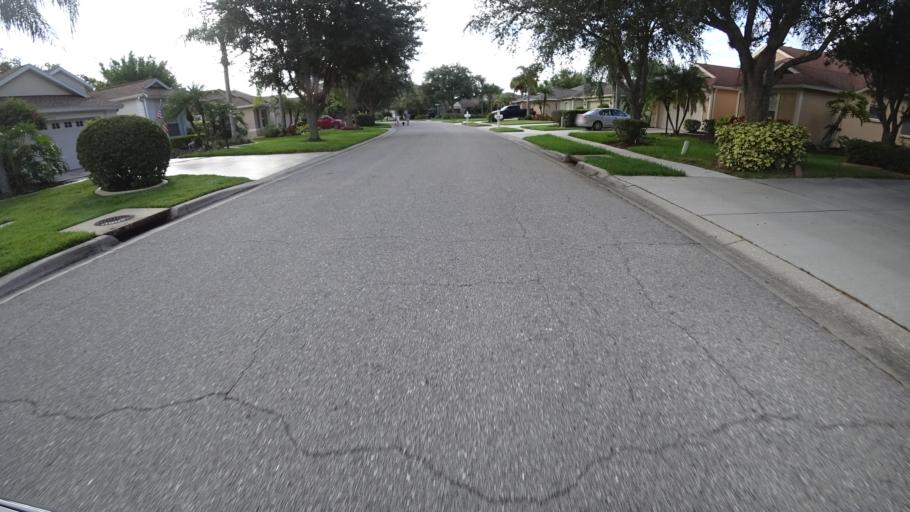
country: US
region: Florida
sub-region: Sarasota County
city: Desoto Lakes
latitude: 27.4232
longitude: -82.4948
